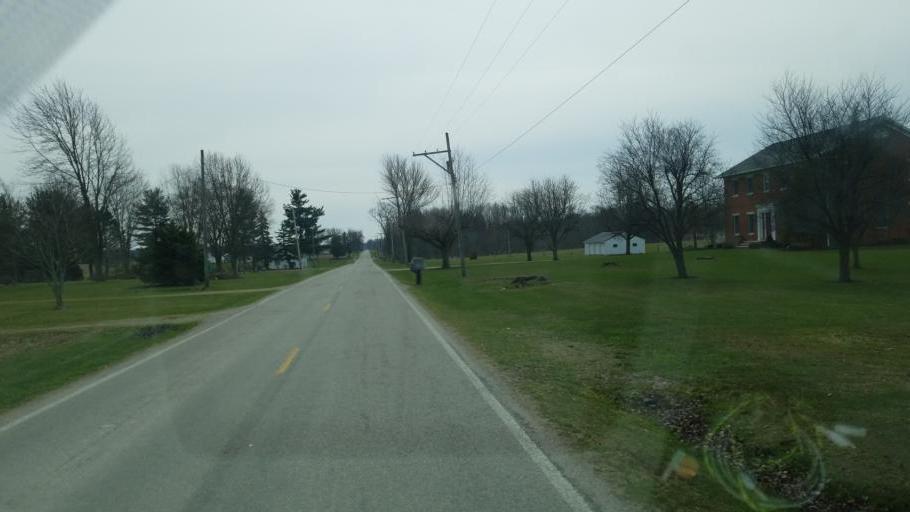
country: US
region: Ohio
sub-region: Huron County
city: New London
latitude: 41.1657
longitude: -82.4901
